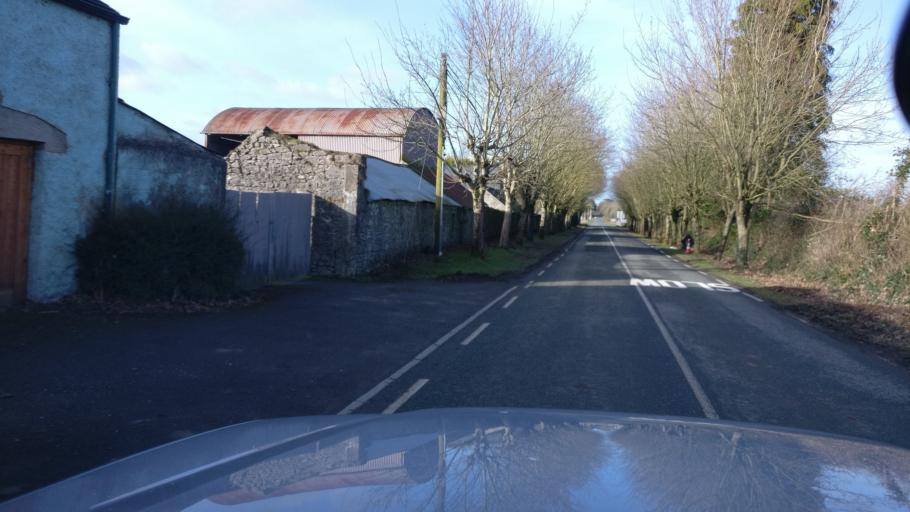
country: IE
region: Leinster
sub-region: Laois
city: Stradbally
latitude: 52.9615
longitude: -7.2019
